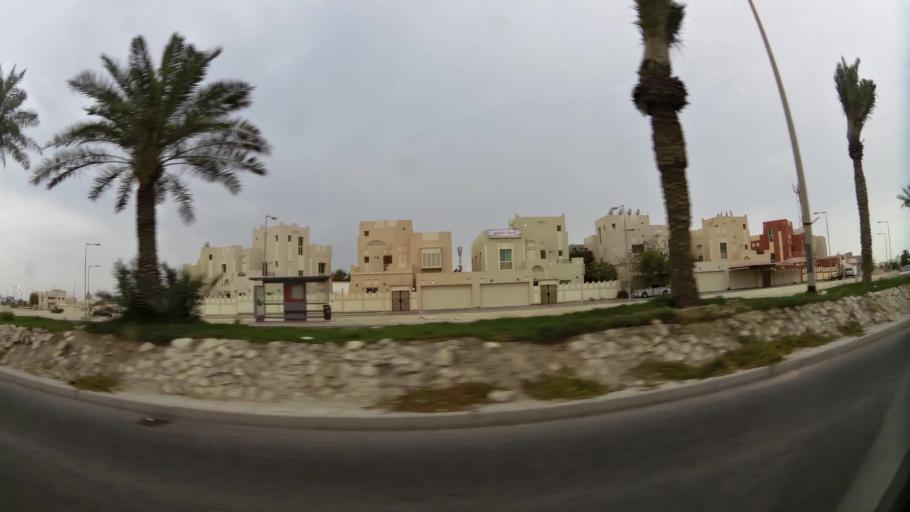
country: BH
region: Central Governorate
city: Madinat Hamad
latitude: 26.1063
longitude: 50.5052
